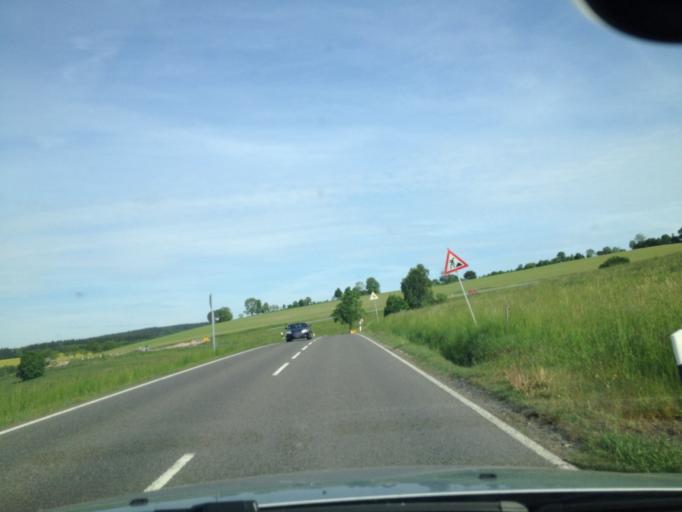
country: DE
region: Saxony
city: Ehrenfriedersdorf
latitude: 50.6262
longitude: 12.9724
